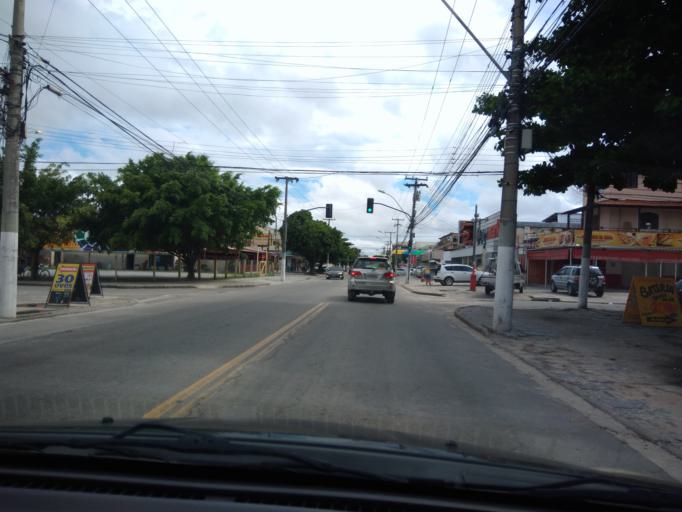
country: BR
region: Rio de Janeiro
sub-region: Niteroi
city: Niteroi
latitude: -22.9425
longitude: -43.0293
